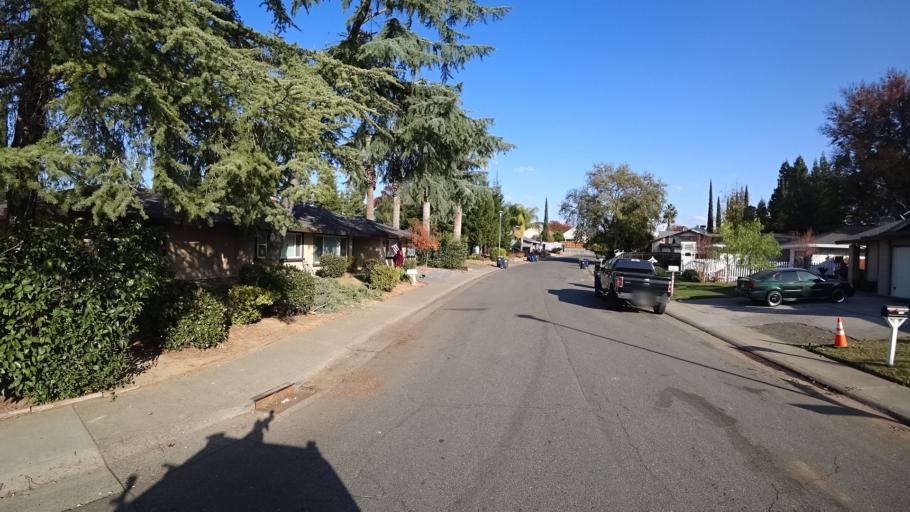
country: US
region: California
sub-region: Sacramento County
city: Citrus Heights
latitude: 38.6934
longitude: -121.2740
